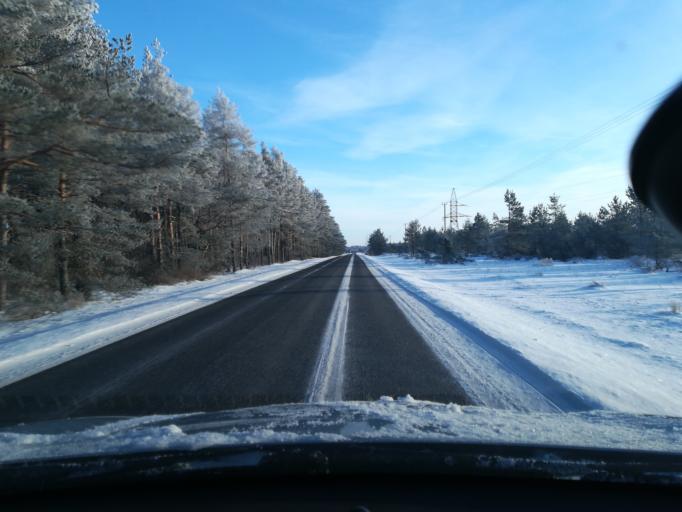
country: EE
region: Harju
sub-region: Keila linn
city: Keila
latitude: 59.3930
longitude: 24.3877
